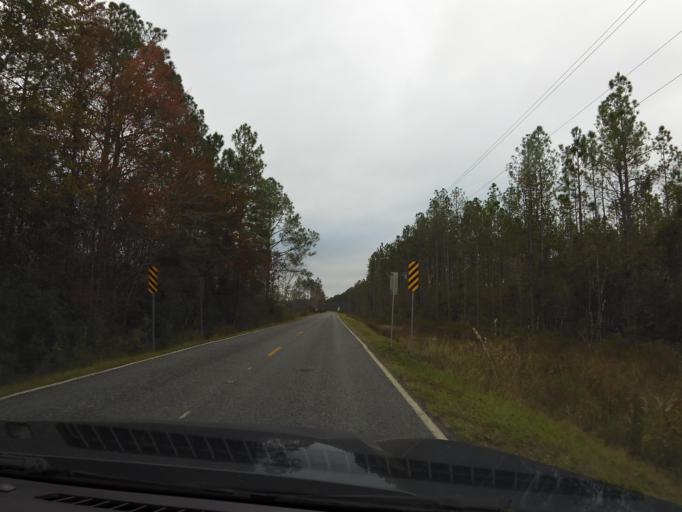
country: US
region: Georgia
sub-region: Charlton County
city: Folkston
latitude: 30.8706
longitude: -82.0436
